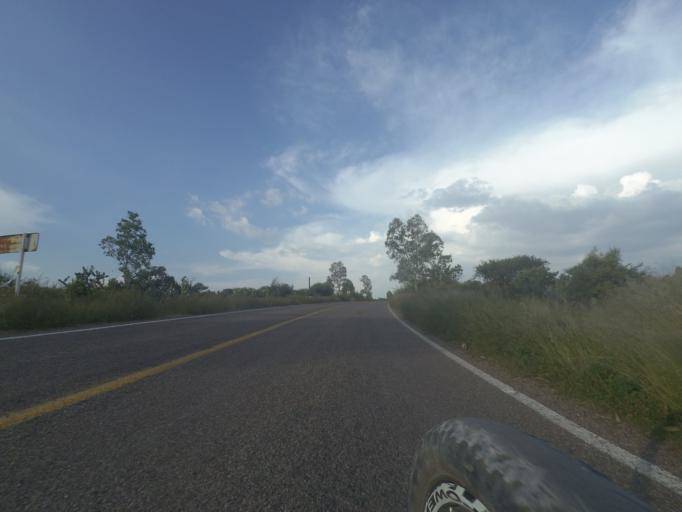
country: MX
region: Aguascalientes
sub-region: Aguascalientes
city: Los Canos
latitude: 21.7812
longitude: -102.3774
